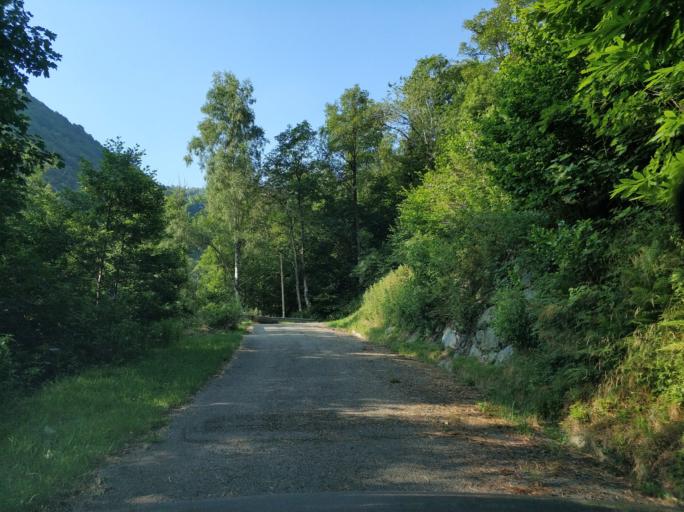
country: IT
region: Piedmont
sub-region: Provincia di Torino
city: Ceres
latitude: 45.3127
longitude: 7.3692
